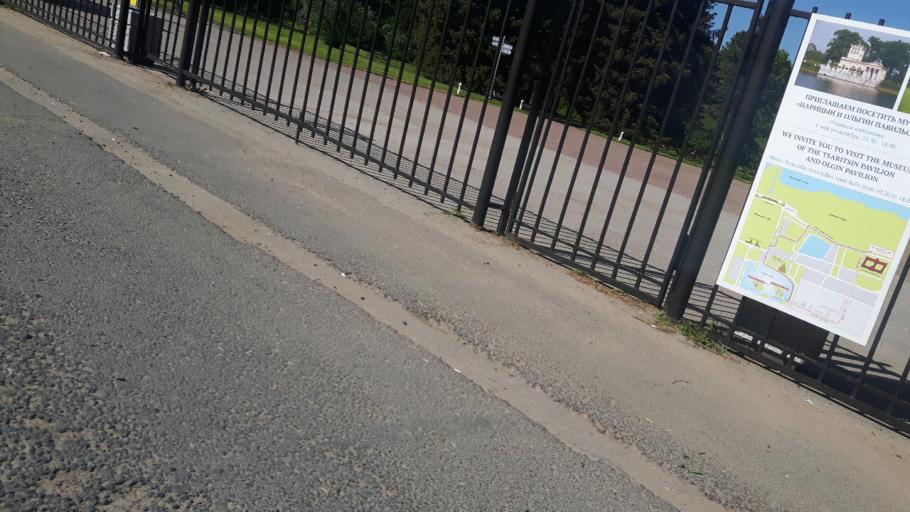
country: RU
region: St.-Petersburg
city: Peterhof
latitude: 59.8807
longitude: 29.9247
